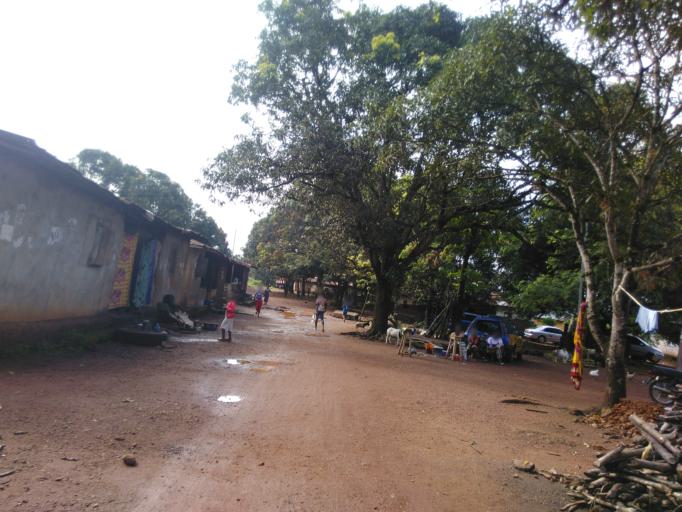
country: SL
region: Southern Province
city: Rotifunk
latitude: 8.4885
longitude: -12.7568
